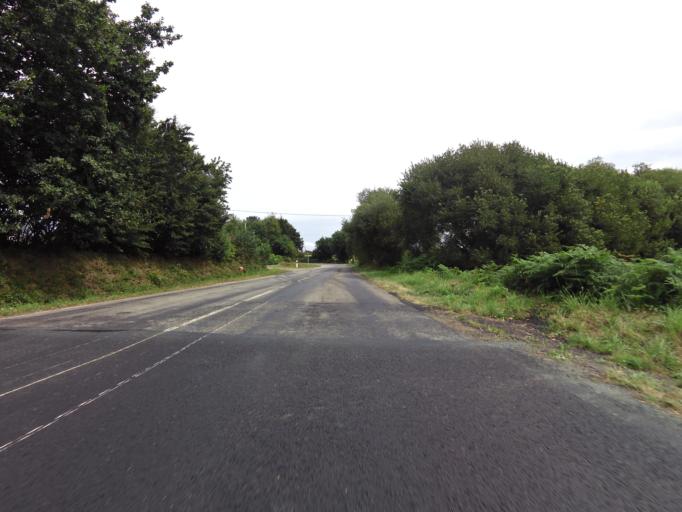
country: FR
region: Brittany
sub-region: Departement du Finistere
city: Poullan-sur-Mer
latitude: 48.0755
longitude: -4.4526
